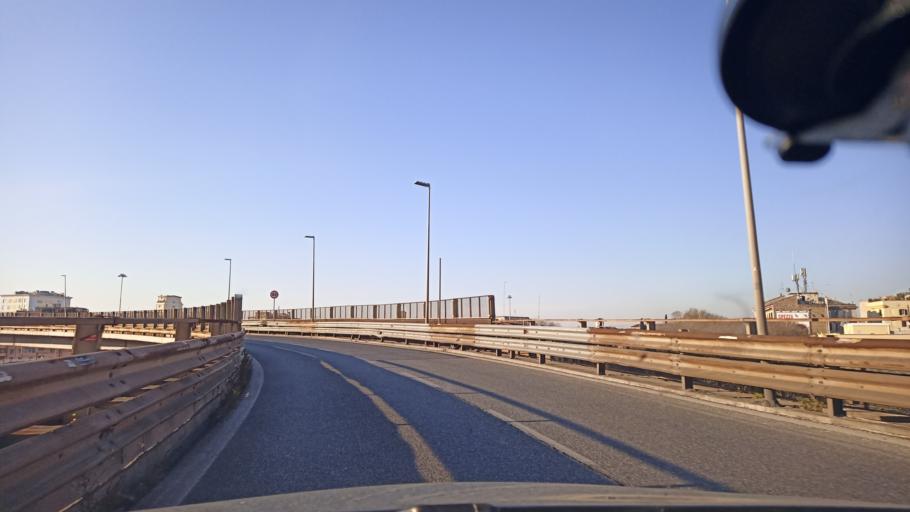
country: IT
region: Latium
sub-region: Citta metropolitana di Roma Capitale
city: Rome
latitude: 41.8947
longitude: 12.5174
